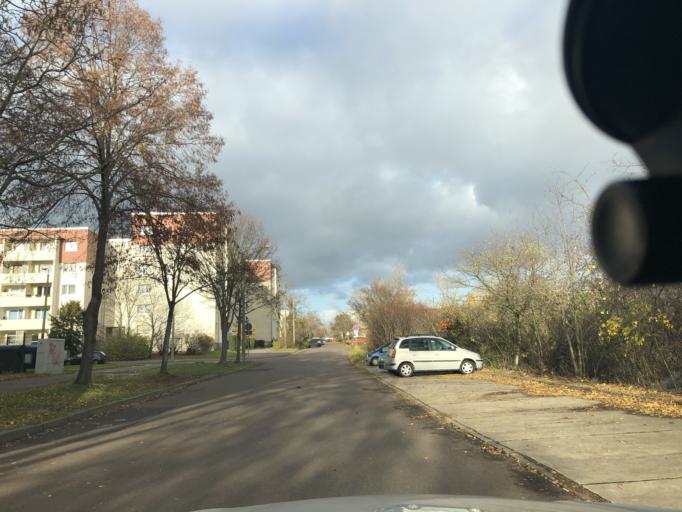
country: DE
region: Saxony-Anhalt
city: Halle Neustadt
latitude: 51.4734
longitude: 11.9081
